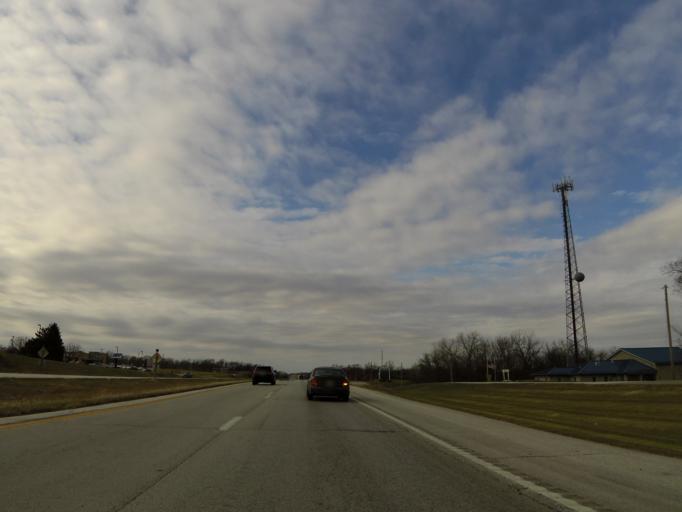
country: US
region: Missouri
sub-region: Marion County
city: Hannibal
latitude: 39.7302
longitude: -91.3977
